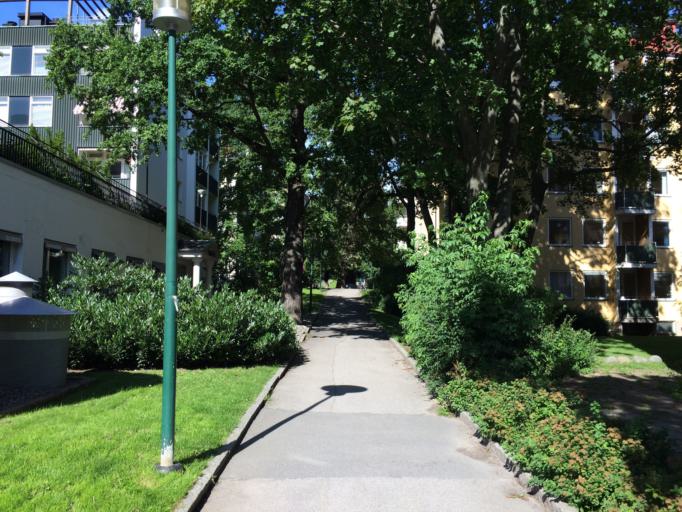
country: SE
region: Stockholm
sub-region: Stockholms Kommun
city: OEstermalm
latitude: 59.3442
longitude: 18.0903
